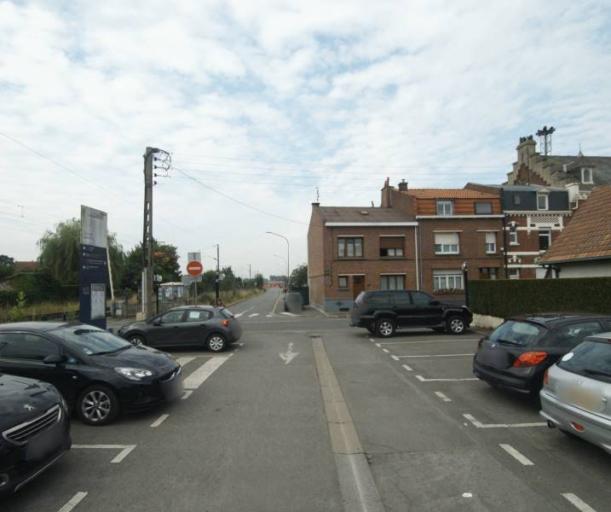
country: FR
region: Nord-Pas-de-Calais
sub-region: Departement du Nord
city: Santes
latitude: 50.5917
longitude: 2.9617
